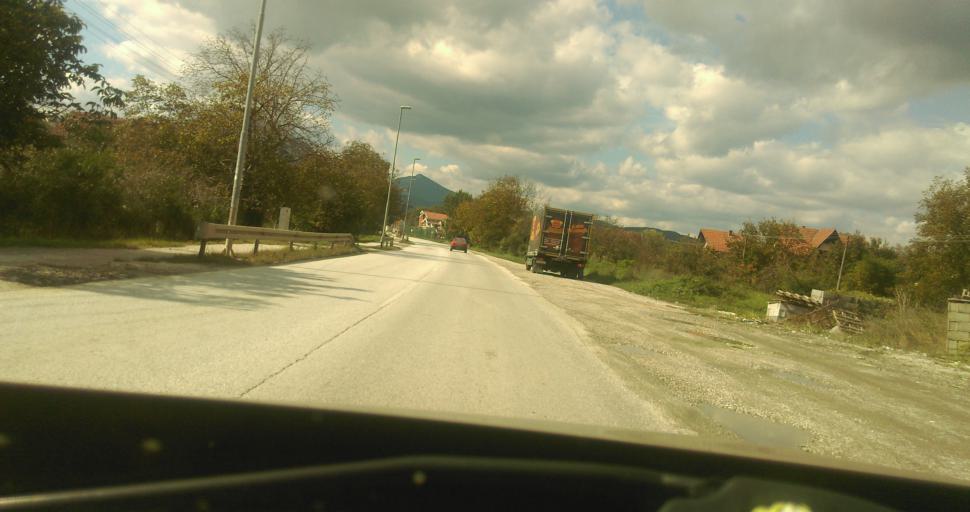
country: RS
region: Central Serbia
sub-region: Moravicki Okrug
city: Cacak
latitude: 43.8959
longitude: 20.2964
